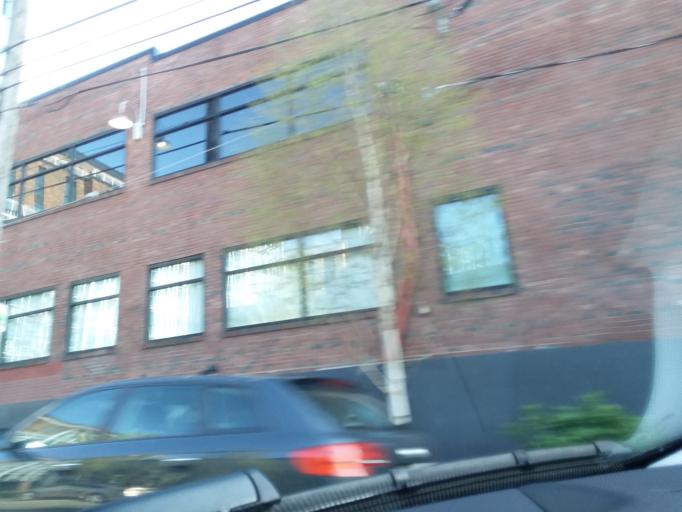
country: US
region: Washington
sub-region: King County
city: Seattle
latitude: 47.6243
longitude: -122.3309
